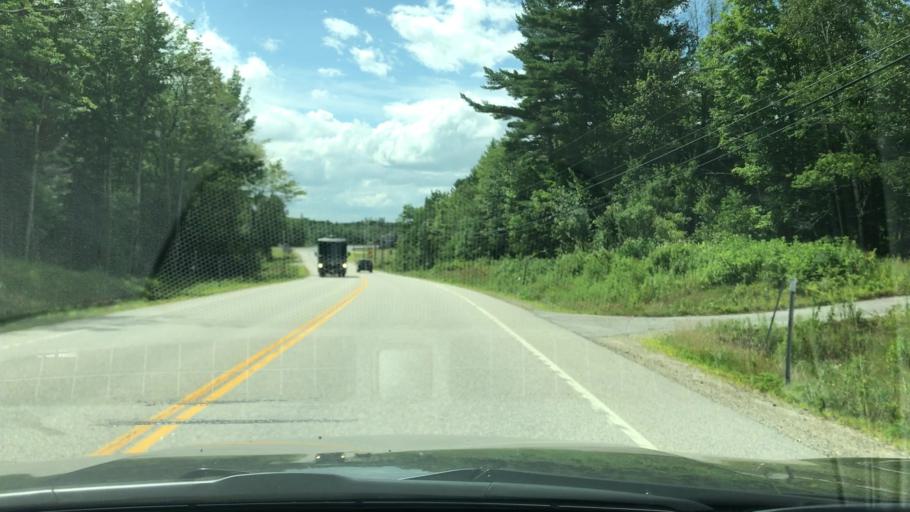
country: US
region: New Hampshire
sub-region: Coos County
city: Jefferson
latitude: 44.3590
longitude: -71.3617
